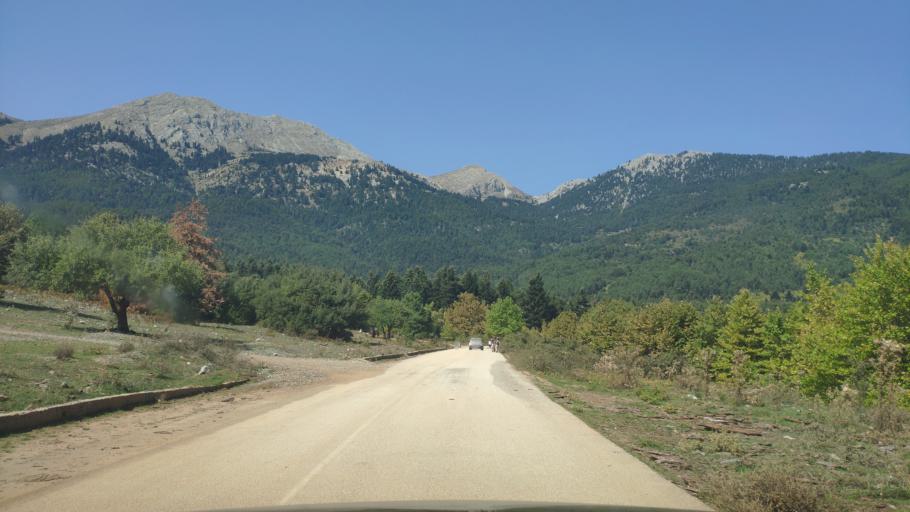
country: GR
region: West Greece
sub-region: Nomos Achaias
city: Kalavryta
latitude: 37.9268
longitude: 22.2809
